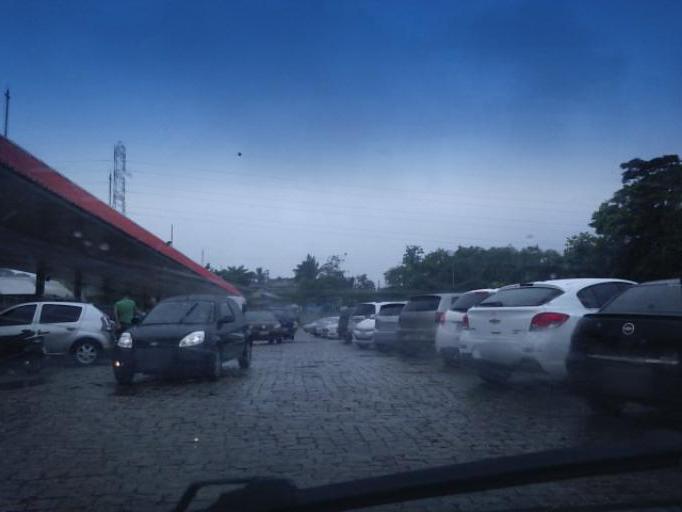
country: BR
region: Sao Paulo
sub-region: Pariquera-Acu
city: Pariquera Acu
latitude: -24.6240
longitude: -47.8960
